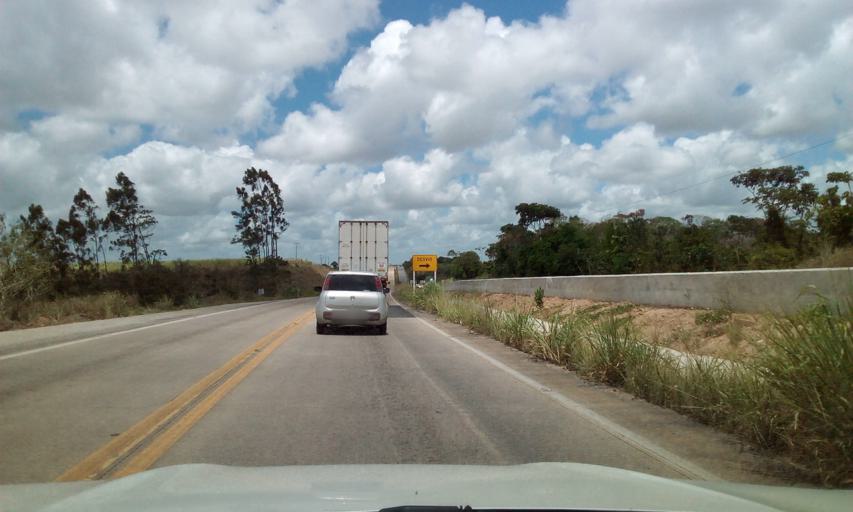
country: BR
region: Alagoas
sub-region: Sao Miguel Dos Campos
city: Sao Miguel dos Campos
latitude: -9.8551
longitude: -36.1443
